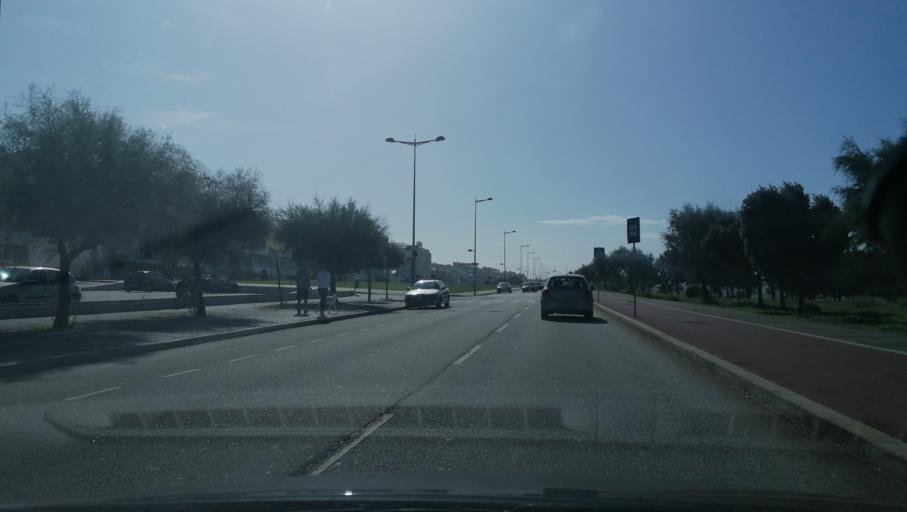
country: PT
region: Aveiro
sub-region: Espinho
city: Espinho
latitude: 41.0244
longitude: -8.6428
